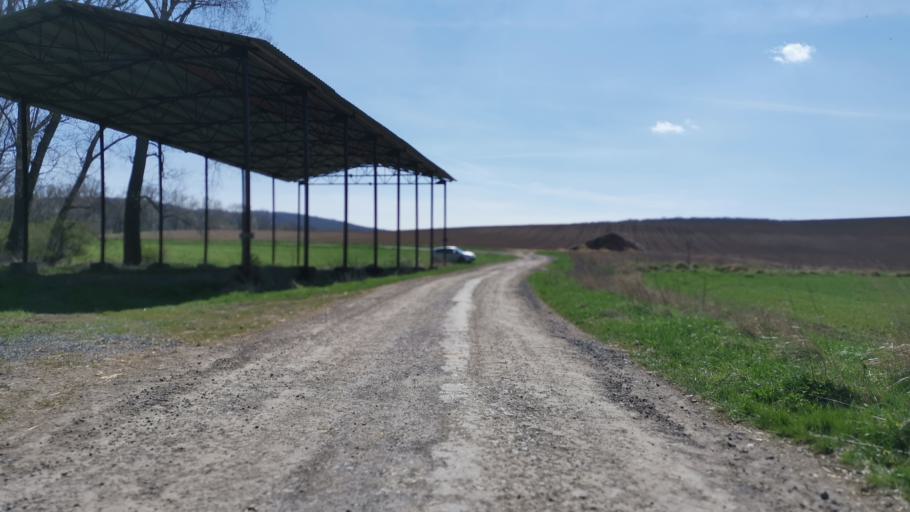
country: SK
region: Trnavsky
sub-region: Okres Skalica
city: Skalica
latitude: 48.7539
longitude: 17.2851
